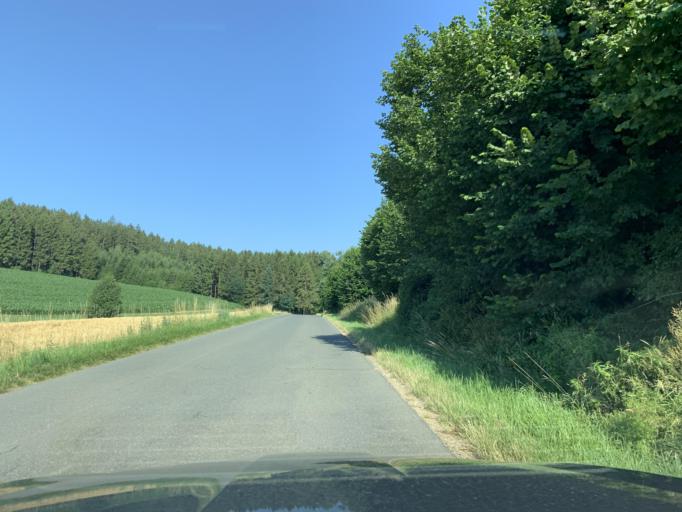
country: DE
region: Bavaria
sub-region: Upper Palatinate
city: Bach
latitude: 49.4049
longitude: 12.3857
